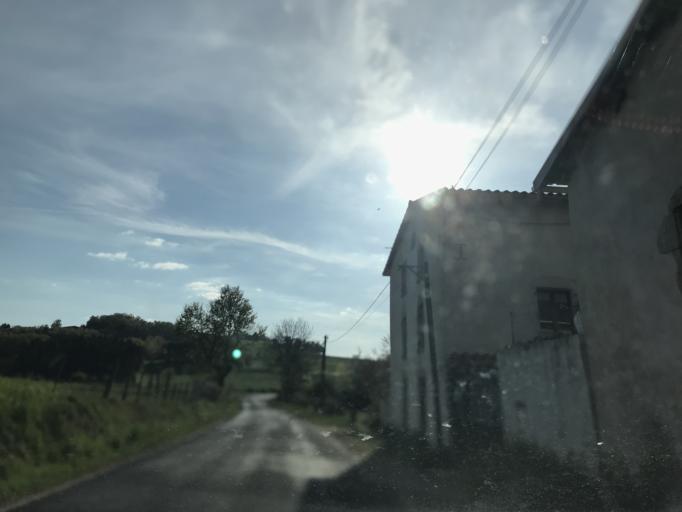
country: FR
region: Auvergne
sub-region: Departement du Puy-de-Dome
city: Courpiere
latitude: 45.7385
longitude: 3.4887
